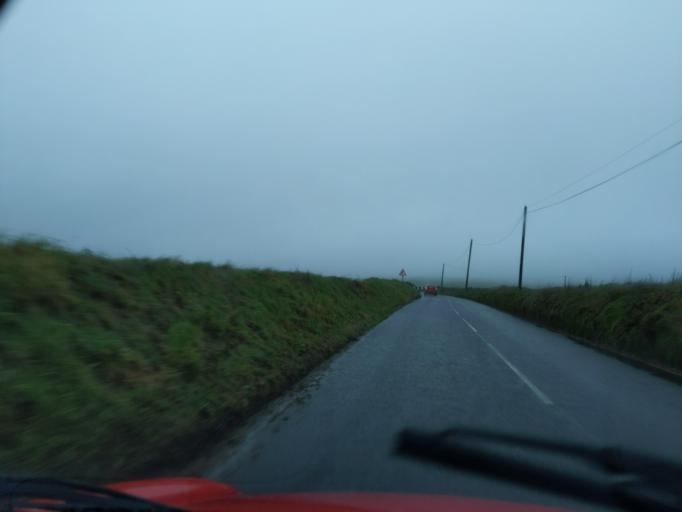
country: GB
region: England
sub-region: Cornwall
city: Camelford
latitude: 50.6425
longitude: -4.6960
